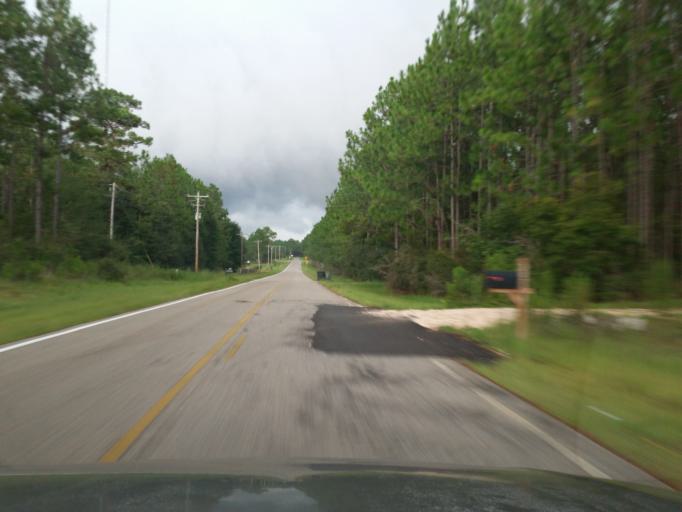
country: US
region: Alabama
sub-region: Baldwin County
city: Robertsdale
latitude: 30.5863
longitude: -87.5623
